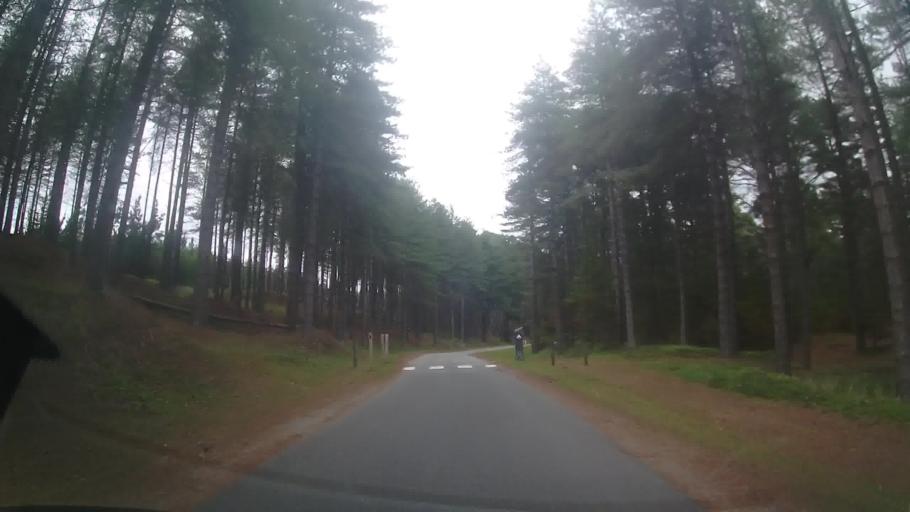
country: GB
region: Wales
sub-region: Gwynedd
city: Caernarfon
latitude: 53.1469
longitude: -4.3853
